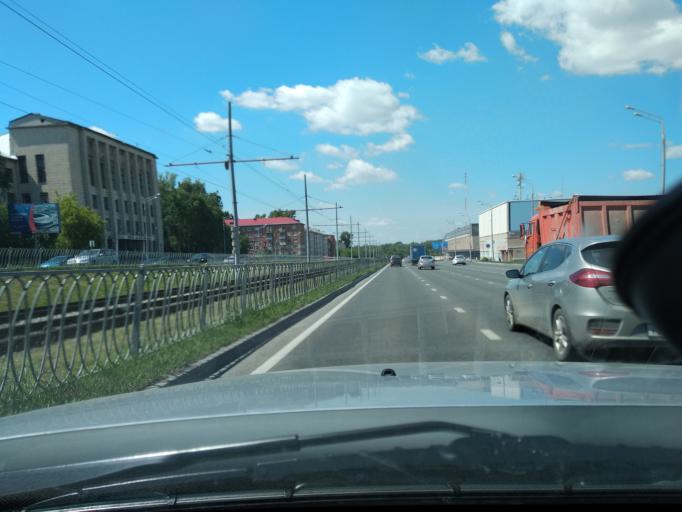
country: RU
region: Tatarstan
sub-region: Gorod Kazan'
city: Kazan
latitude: 55.8142
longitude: 49.1881
